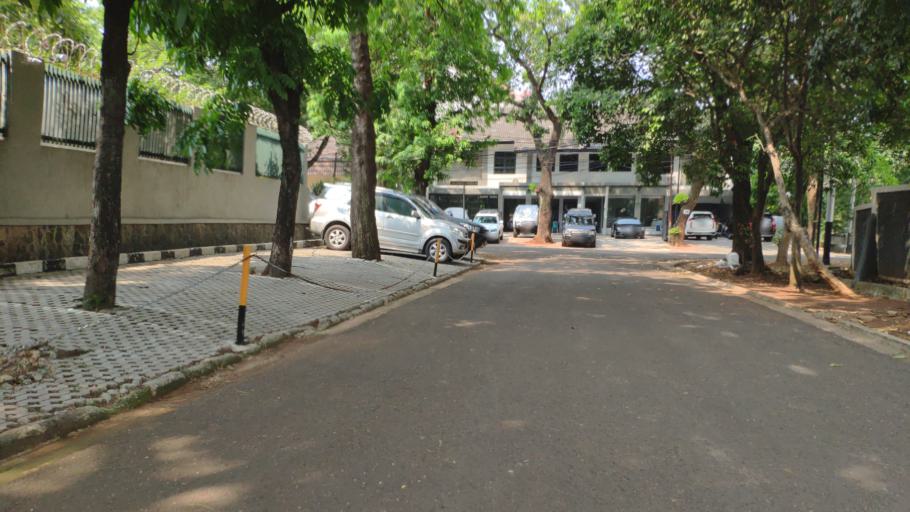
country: ID
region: Jakarta Raya
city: Jakarta
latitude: -6.2505
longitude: 106.8062
